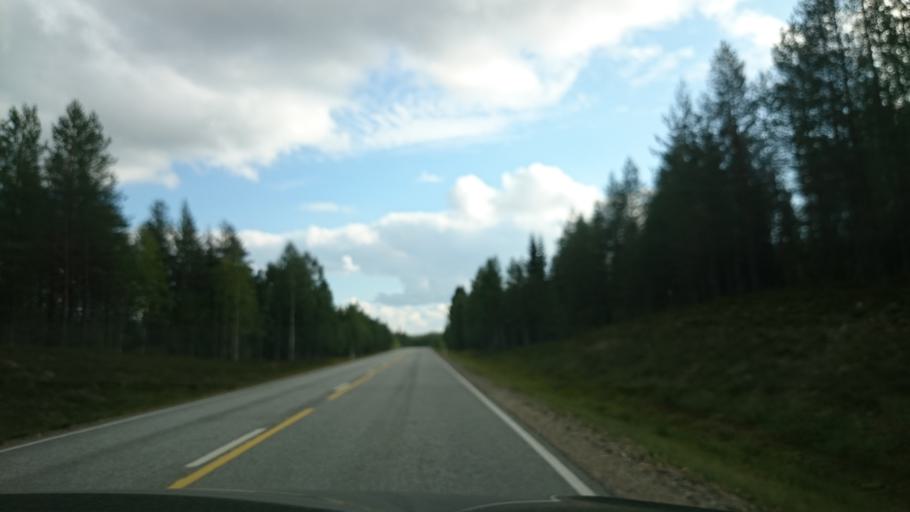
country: FI
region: Kainuu
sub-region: Kehys-Kainuu
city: Kuhmo
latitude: 64.5239
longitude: 29.9457
